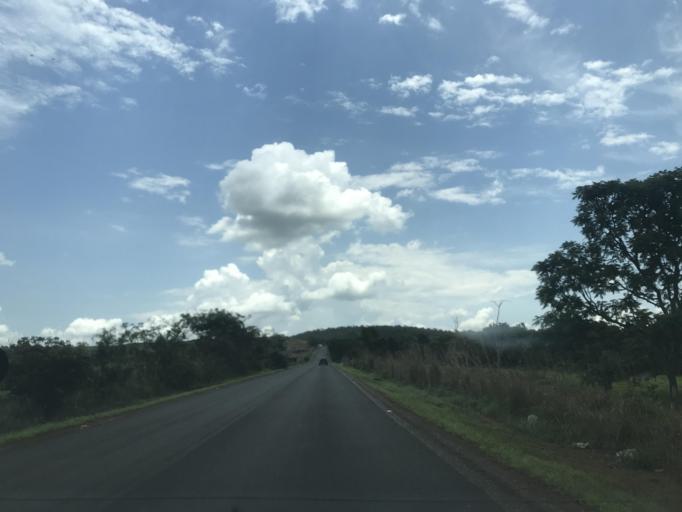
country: BR
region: Goias
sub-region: Vianopolis
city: Vianopolis
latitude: -16.9499
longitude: -48.5913
